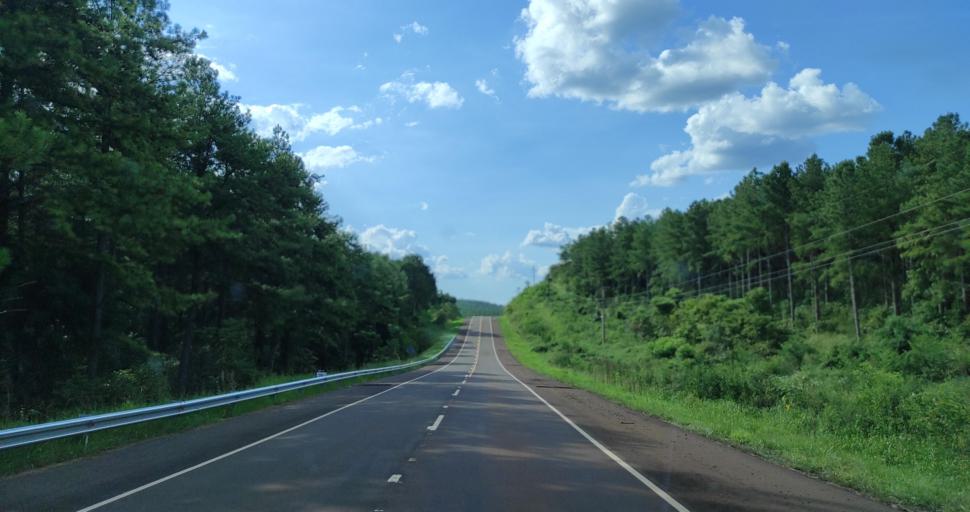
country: AR
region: Misiones
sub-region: Departamento de San Pedro
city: San Pedro
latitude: -26.3593
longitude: -53.9539
